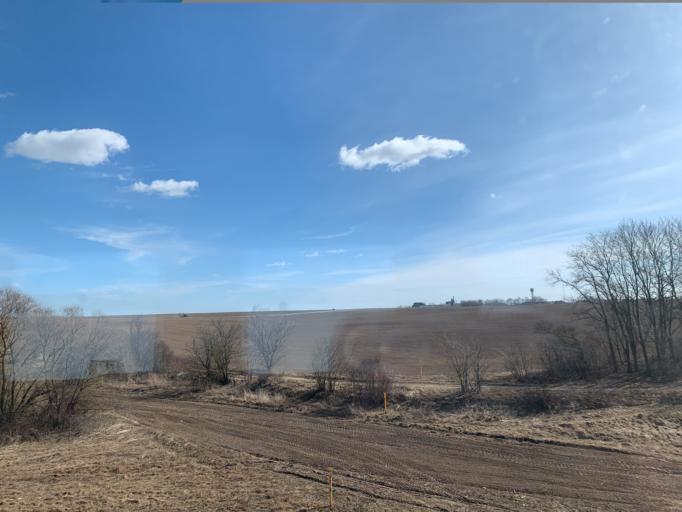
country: BY
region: Minsk
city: Haradzyeya
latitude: 53.3271
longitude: 26.5448
